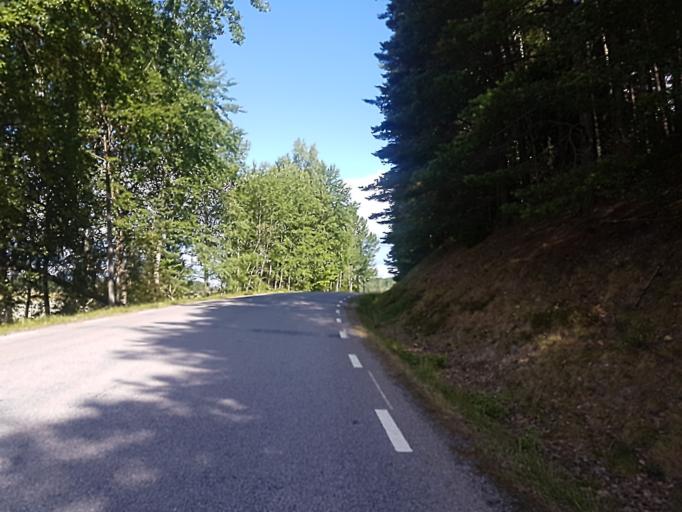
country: SE
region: Soedermanland
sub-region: Gnesta Kommun
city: Gnesta
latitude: 59.0382
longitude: 17.3470
